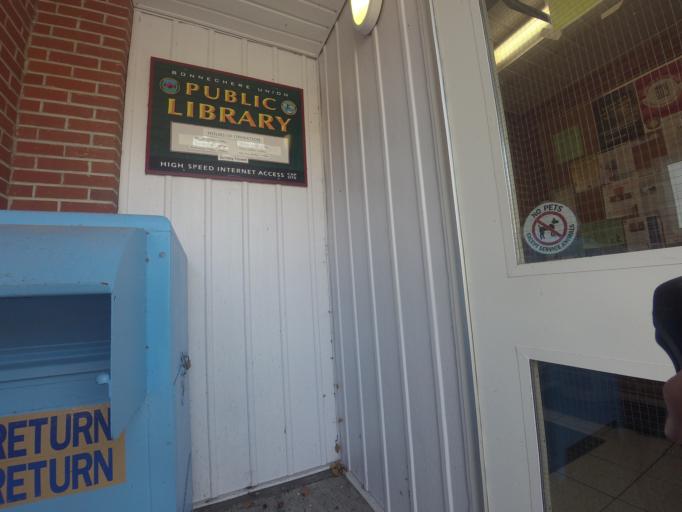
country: CA
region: Ontario
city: Pembroke
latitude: 45.5412
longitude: -77.0972
